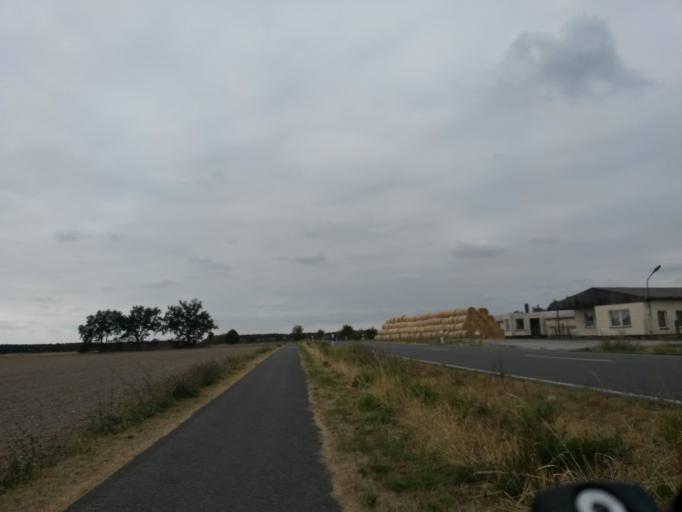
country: DE
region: Saxony-Anhalt
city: Muhlanger
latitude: 51.8654
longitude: 12.7831
